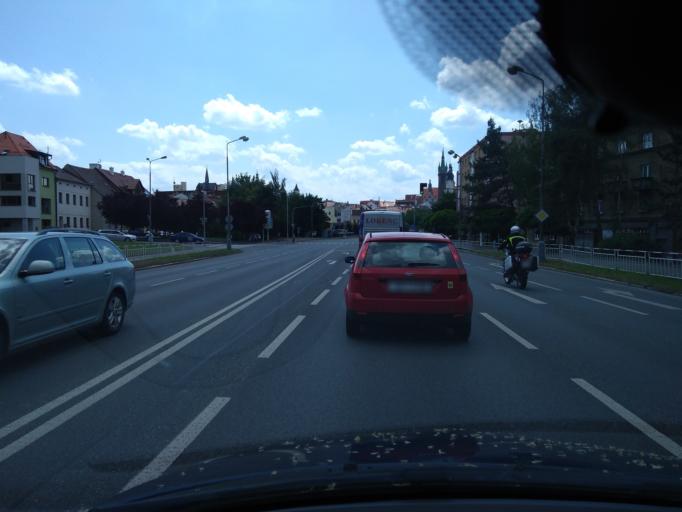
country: CZ
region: Plzensky
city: Klatovy
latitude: 49.4000
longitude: 13.2931
